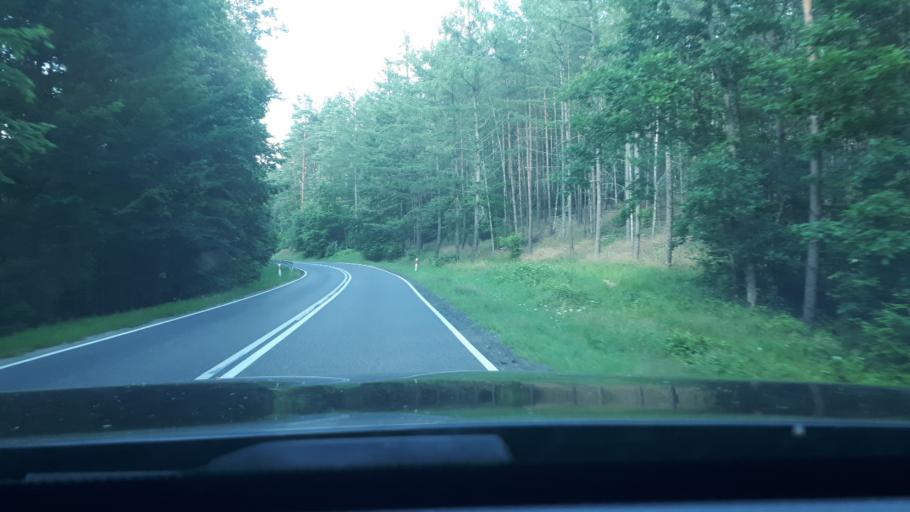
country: PL
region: Warmian-Masurian Voivodeship
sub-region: Powiat olsztynski
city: Stawiguda
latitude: 53.5337
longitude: 20.4610
